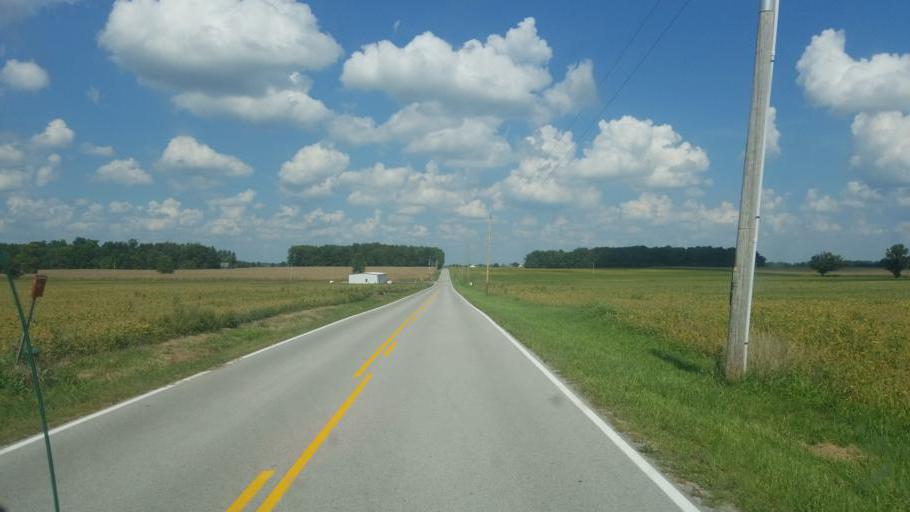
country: US
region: Ohio
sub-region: Hancock County
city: Arlington
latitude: 40.8602
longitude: -83.7275
